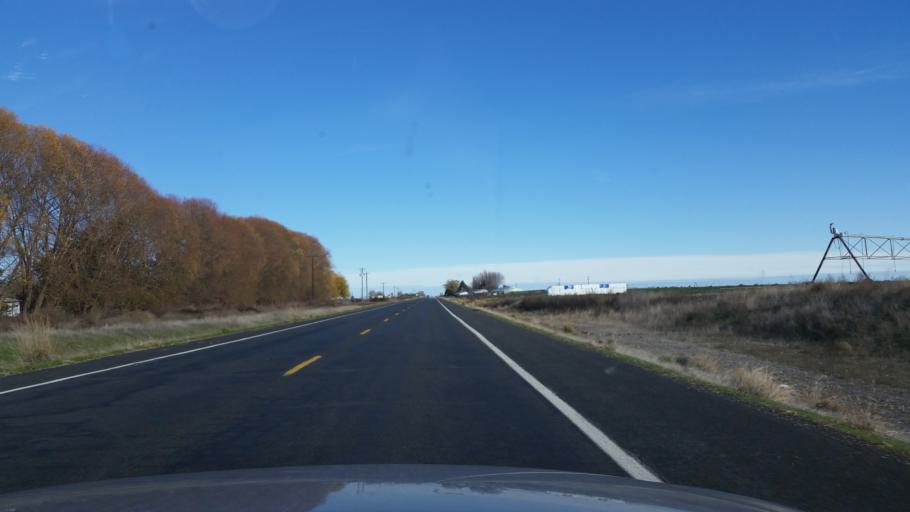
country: US
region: Washington
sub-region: Grant County
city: Ephrata
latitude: 47.1992
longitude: -119.6783
